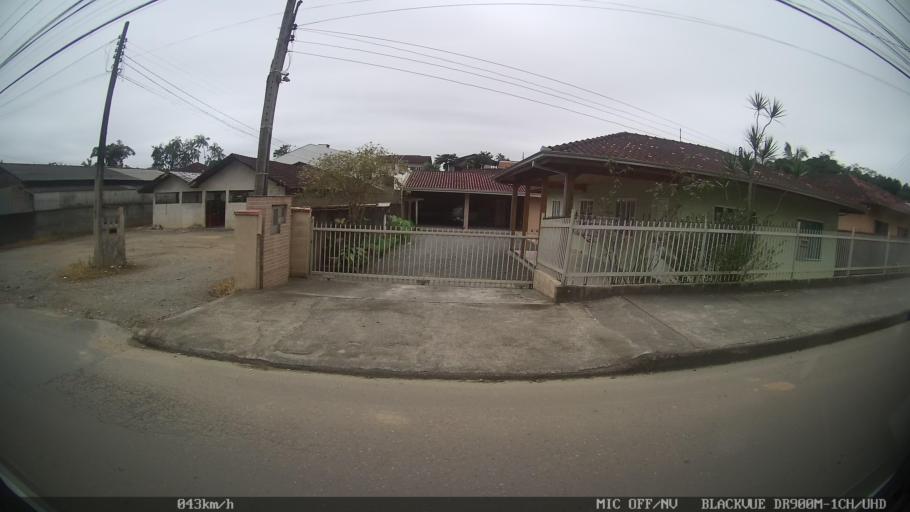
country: BR
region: Santa Catarina
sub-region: Joinville
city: Joinville
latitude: -26.2777
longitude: -48.9121
